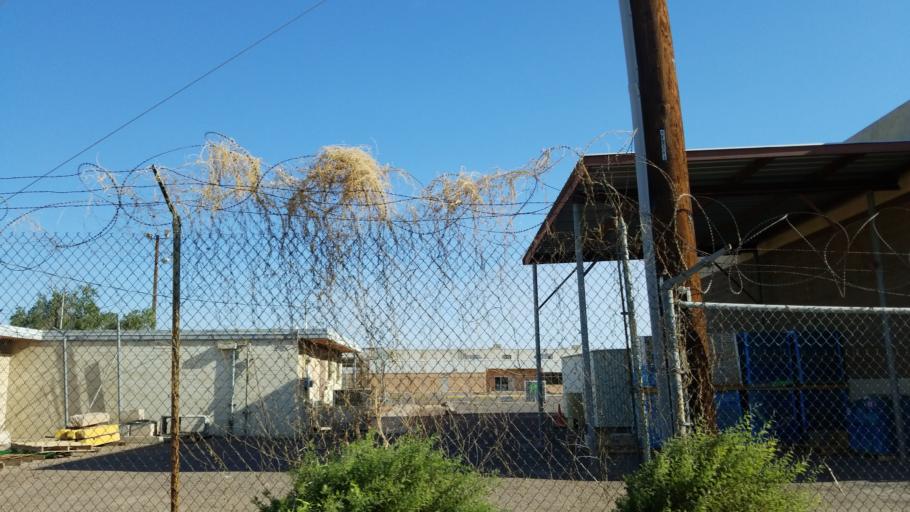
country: US
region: Arizona
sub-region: Maricopa County
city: Phoenix
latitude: 33.4240
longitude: -112.1069
